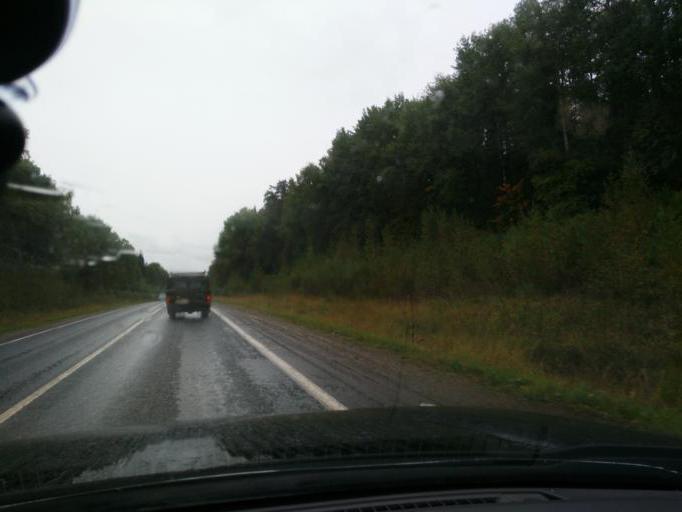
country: RU
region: Perm
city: Yugo-Kamskiy
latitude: 57.6318
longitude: 55.6152
